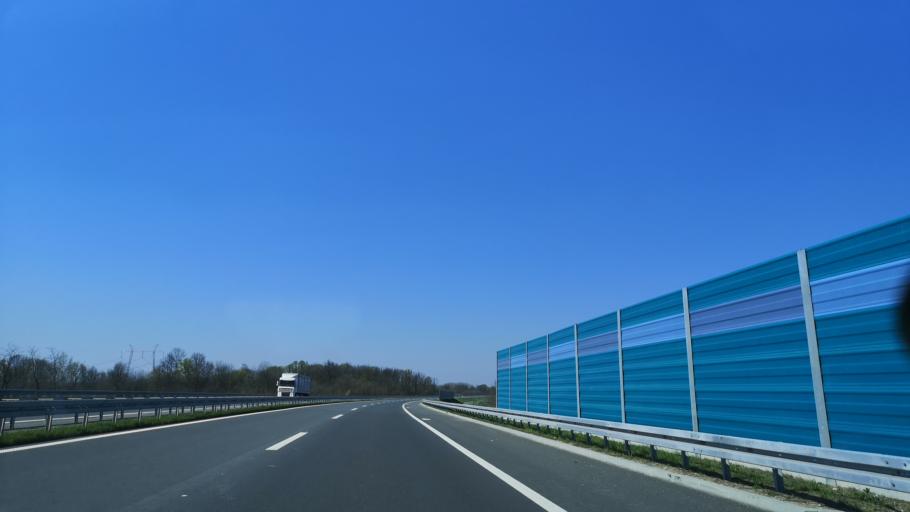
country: RS
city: Zvecka
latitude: 44.6095
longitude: 20.1946
